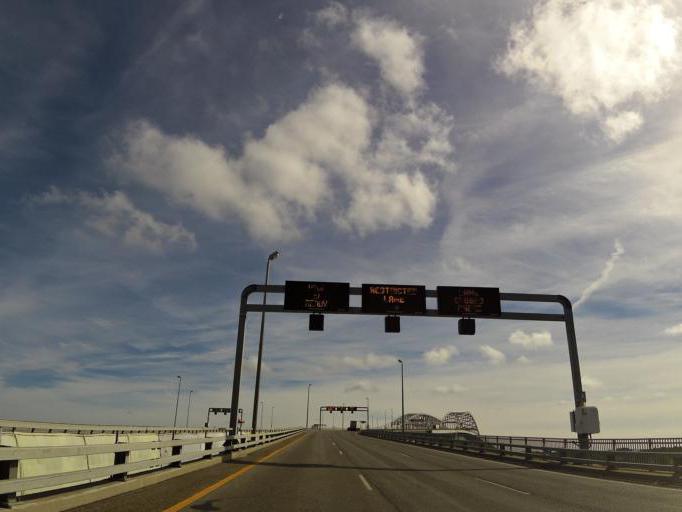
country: US
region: Michigan
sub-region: Saint Clair County
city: Port Huron
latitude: 42.9992
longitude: -82.4307
